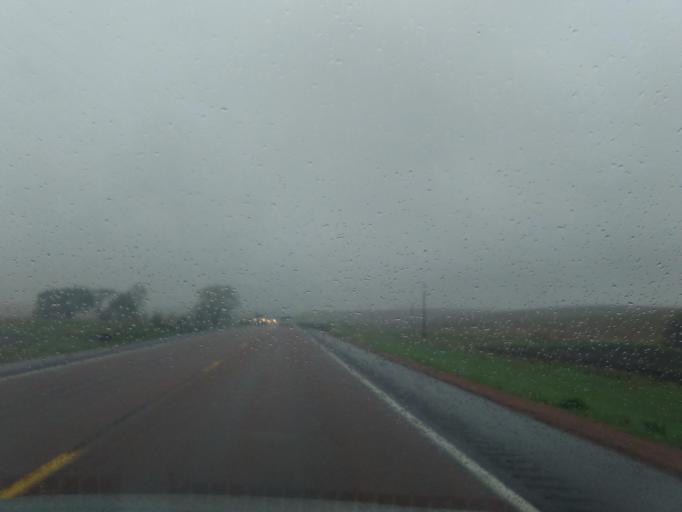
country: US
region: Nebraska
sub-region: Wayne County
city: Wayne
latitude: 42.2357
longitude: -97.1117
